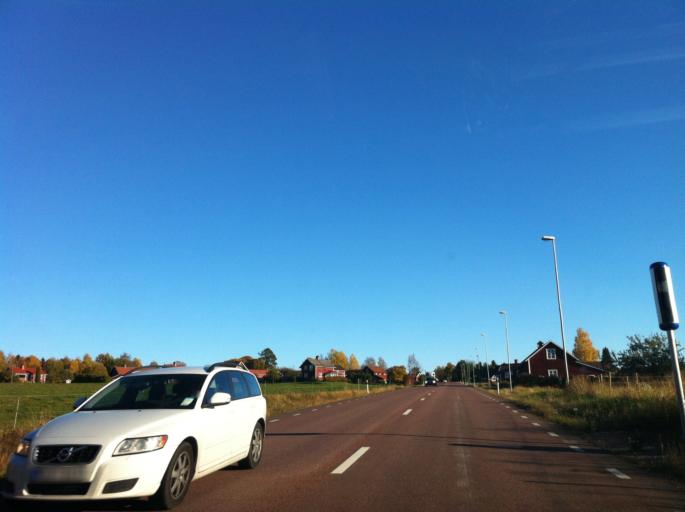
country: SE
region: Dalarna
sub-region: Leksand Municipality
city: Siljansnas
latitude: 60.9259
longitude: 14.8102
